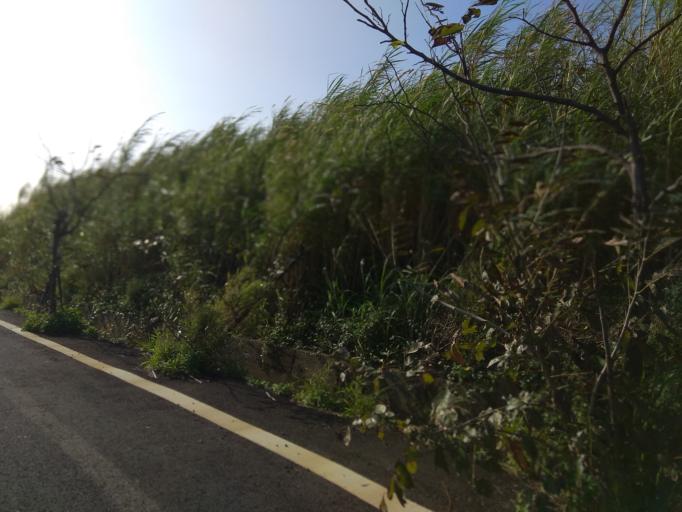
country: TW
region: Taiwan
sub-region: Hsinchu
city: Zhubei
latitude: 25.0062
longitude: 121.0434
